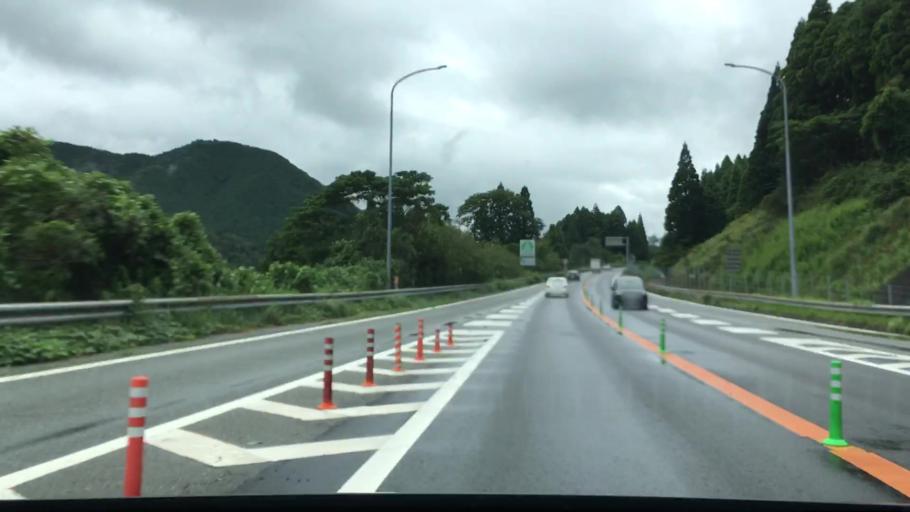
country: JP
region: Hyogo
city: Nishiwaki
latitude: 35.1157
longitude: 134.7845
